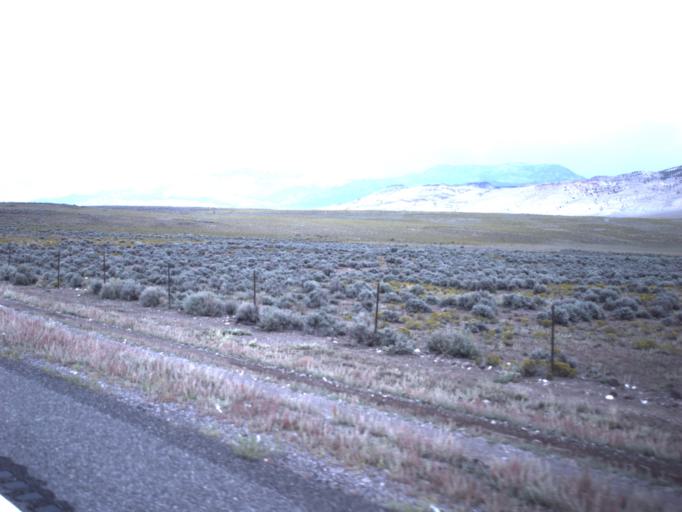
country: US
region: Utah
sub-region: Piute County
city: Junction
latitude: 38.2697
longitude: -112.2224
